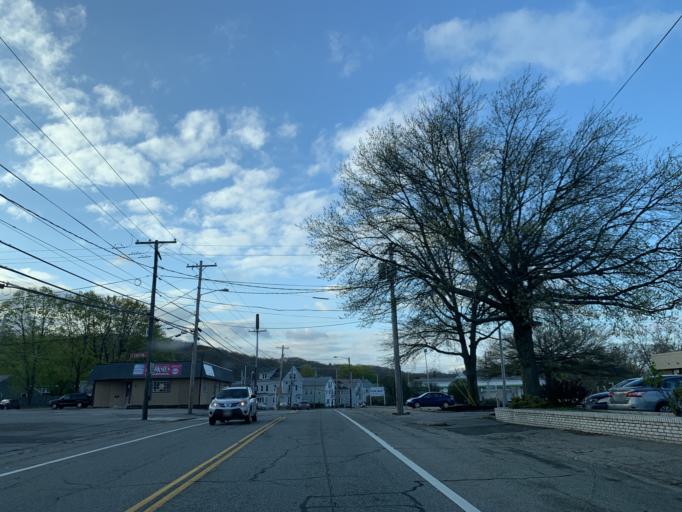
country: US
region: Rhode Island
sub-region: Providence County
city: Central Falls
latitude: 41.8796
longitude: -71.4155
